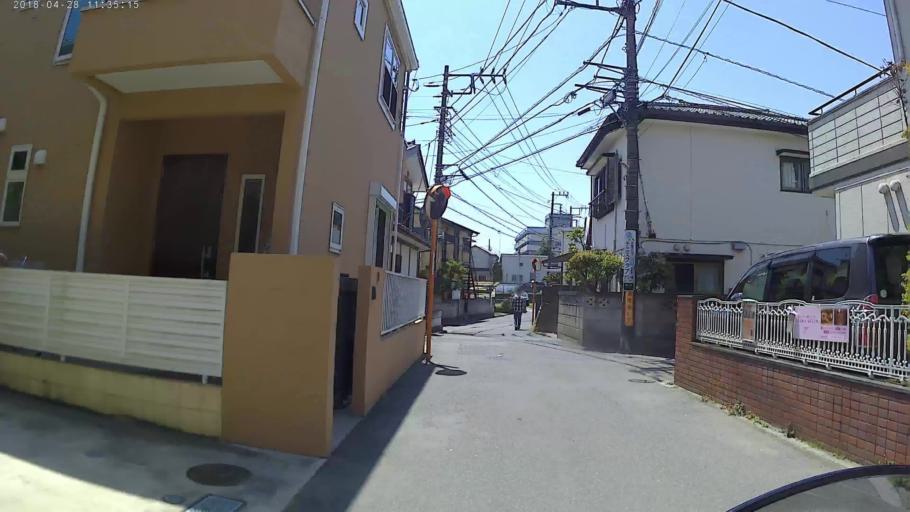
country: JP
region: Kanagawa
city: Fujisawa
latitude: 35.3449
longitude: 139.4510
